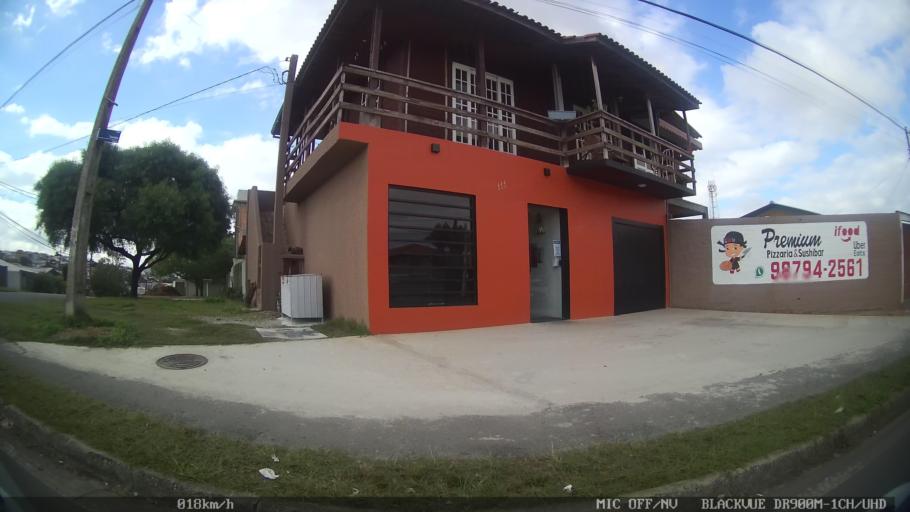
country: BR
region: Parana
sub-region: Colombo
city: Colombo
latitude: -25.3603
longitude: -49.1909
